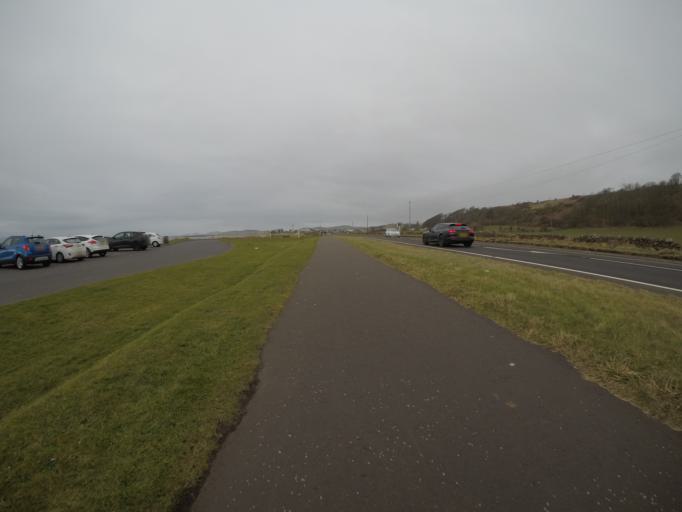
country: GB
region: Scotland
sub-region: North Ayrshire
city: West Kilbride
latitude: 55.6711
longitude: -4.8470
